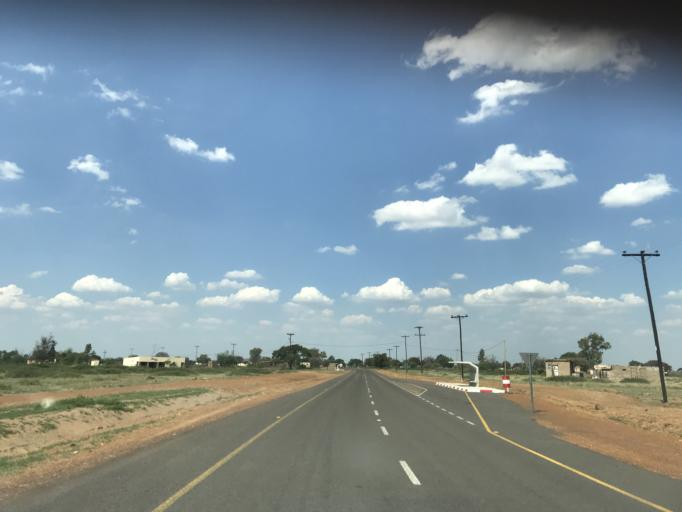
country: BW
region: South East
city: Janeng
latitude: -25.5630
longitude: 25.5897
